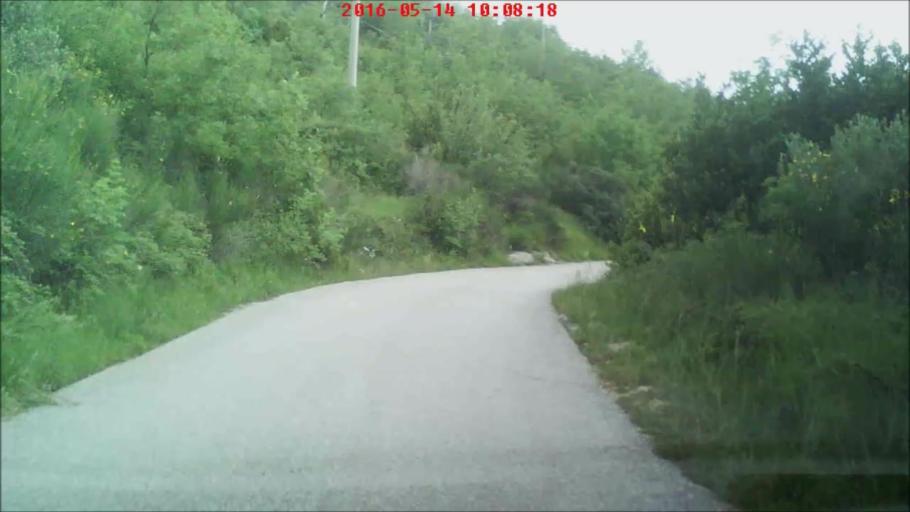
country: HR
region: Dubrovacko-Neretvanska
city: Podgora
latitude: 42.7489
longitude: 17.9350
